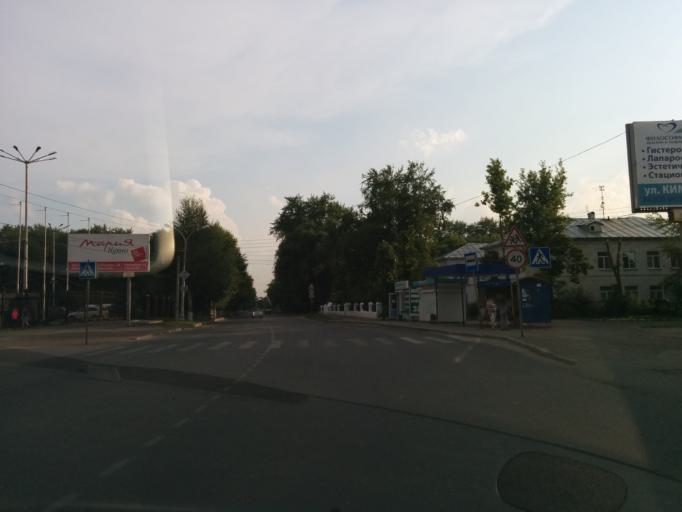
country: RU
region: Perm
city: Perm
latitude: 58.0253
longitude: 56.2950
